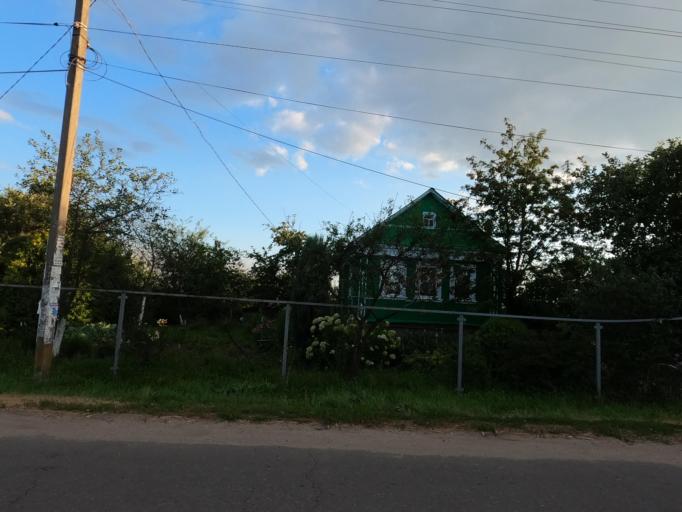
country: RU
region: Moskovskaya
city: Ashitkovo
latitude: 55.4207
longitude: 38.5722
